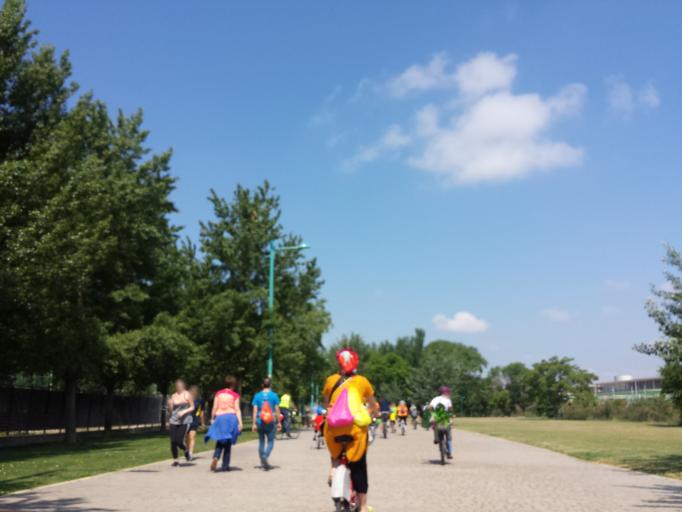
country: ES
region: Aragon
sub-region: Provincia de Zaragoza
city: Almozara
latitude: 41.6652
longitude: -0.8975
